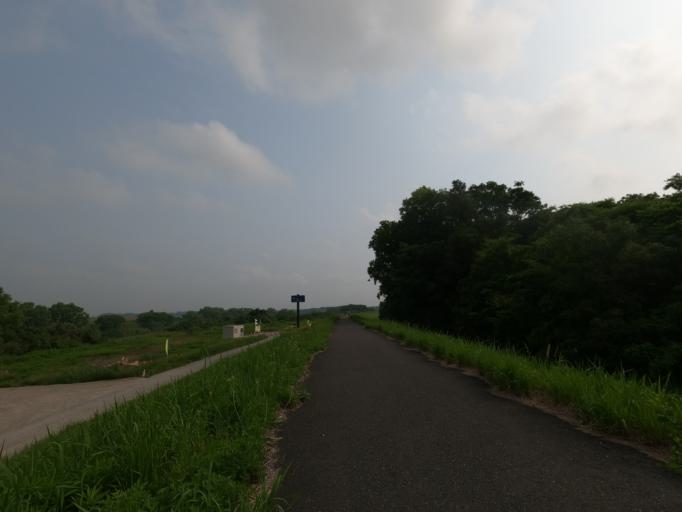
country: JP
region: Ibaraki
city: Moriya
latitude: 35.9540
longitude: 139.9468
